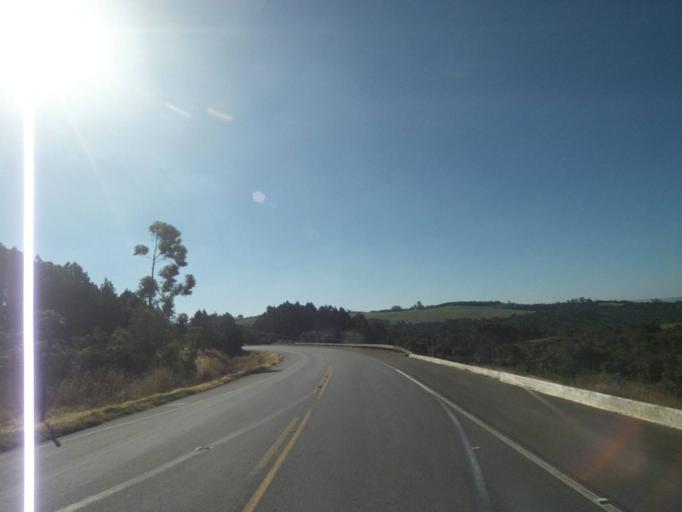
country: BR
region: Parana
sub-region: Tibagi
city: Tibagi
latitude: -24.7927
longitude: -50.4660
